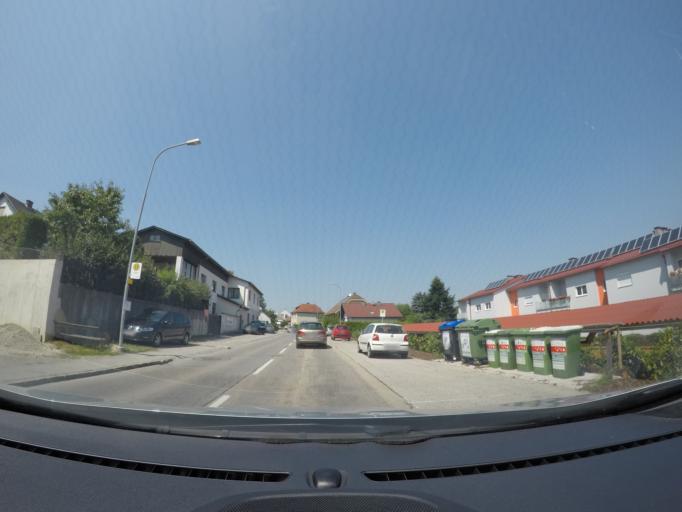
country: AT
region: Lower Austria
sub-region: Politischer Bezirk Sankt Polten
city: Maria-Anzbach
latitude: 48.1896
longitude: 15.9341
